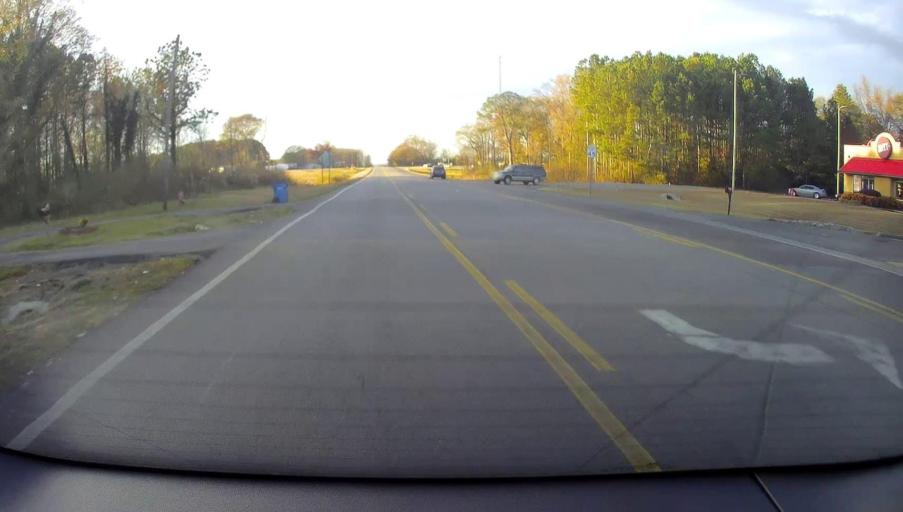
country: US
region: Alabama
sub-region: Blount County
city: Oneonta
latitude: 34.1210
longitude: -86.3972
